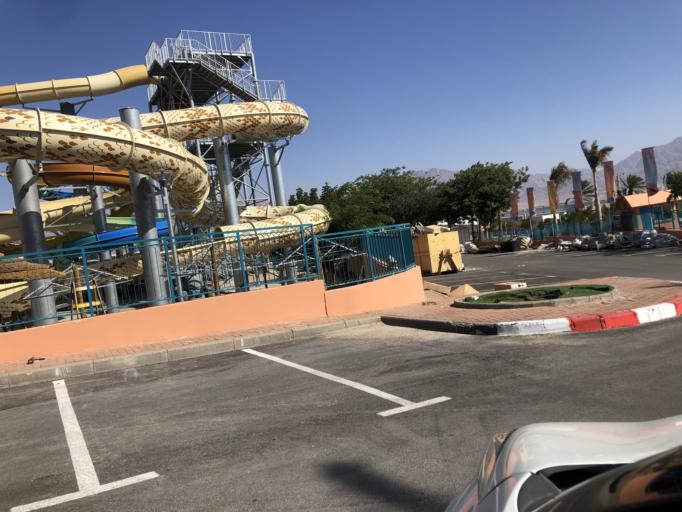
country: IL
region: Southern District
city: Eilat
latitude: 29.5800
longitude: 34.9633
